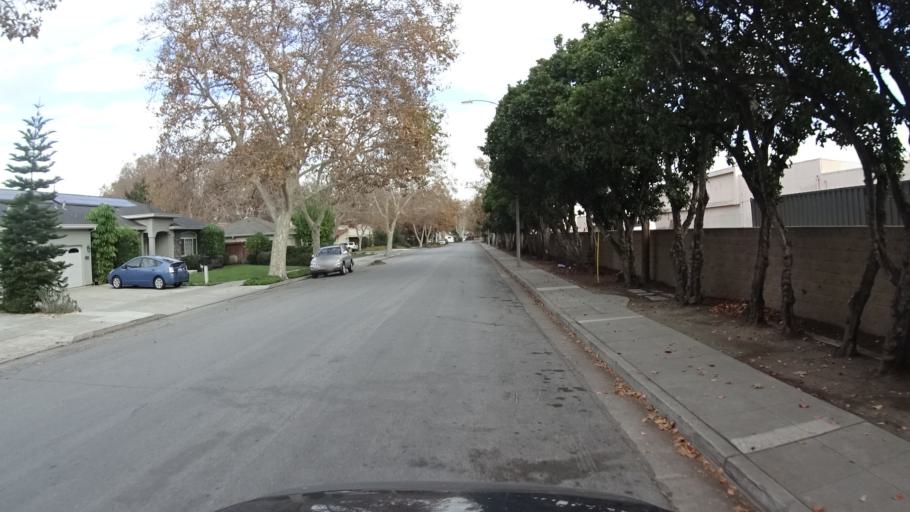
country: US
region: California
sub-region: Santa Clara County
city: Buena Vista
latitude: 37.3244
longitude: -121.9233
